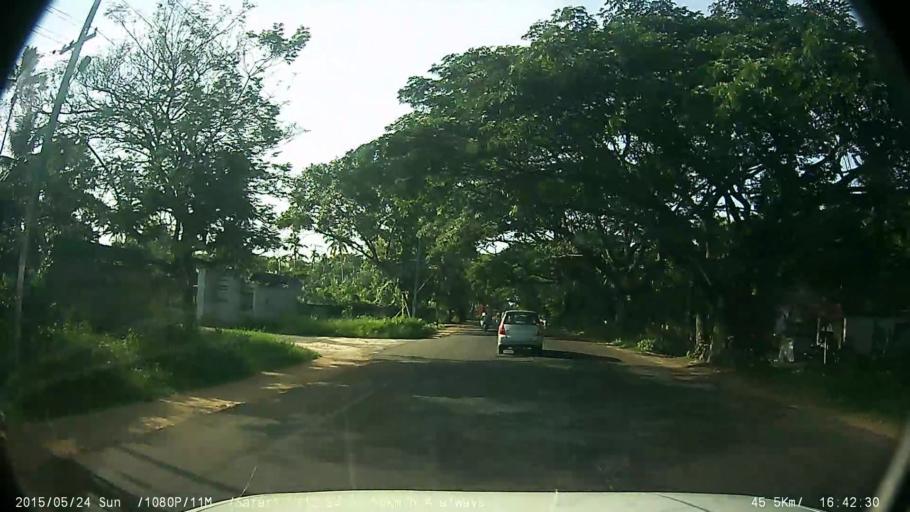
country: IN
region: Kerala
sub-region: Alappuzha
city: Shertallai
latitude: 9.6413
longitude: 76.3352
